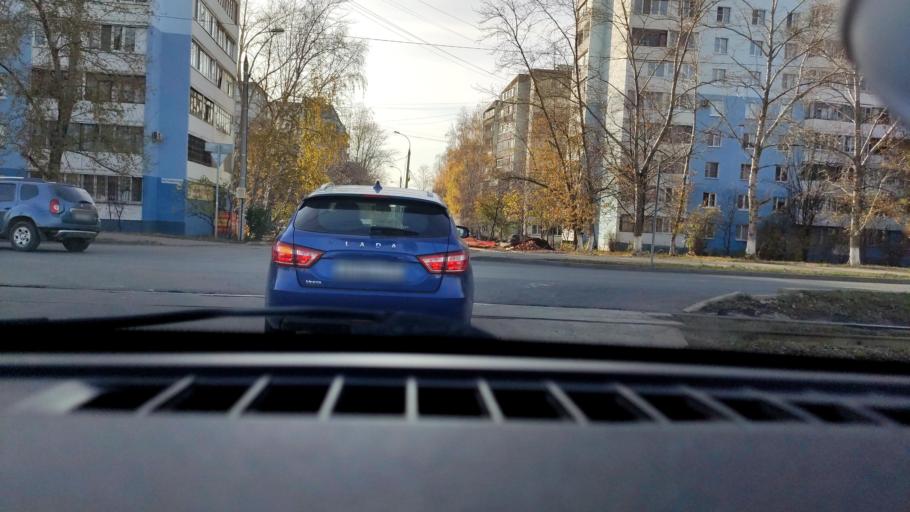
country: RU
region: Samara
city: Samara
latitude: 53.2626
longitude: 50.2365
